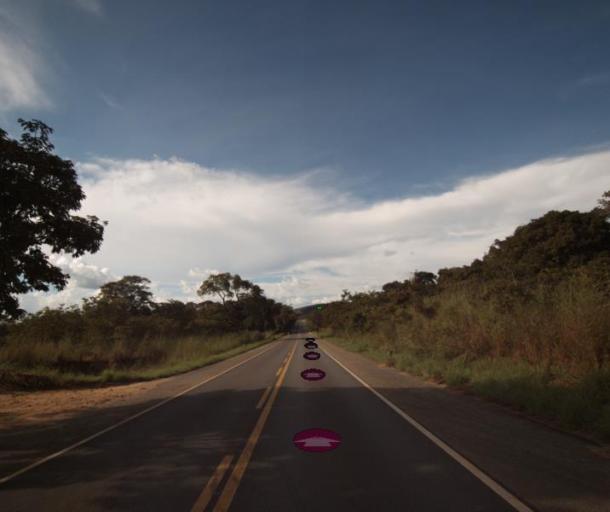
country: BR
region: Goias
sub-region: Barro Alto
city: Barro Alto
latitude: -14.9925
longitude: -48.6816
